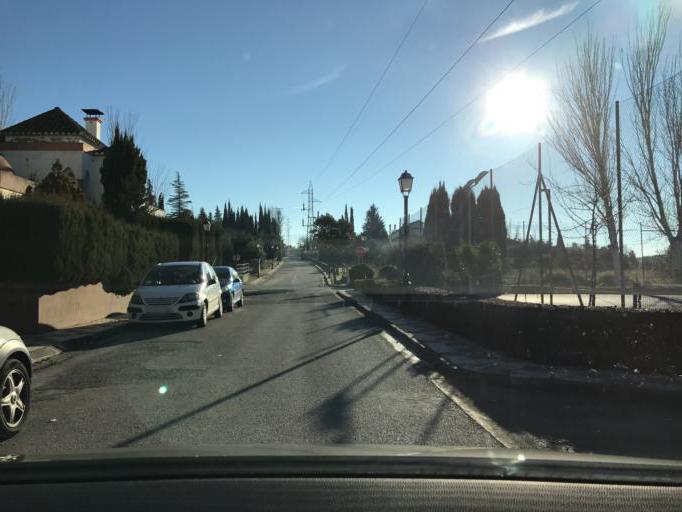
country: ES
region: Andalusia
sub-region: Provincia de Granada
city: Albolote
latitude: 37.2510
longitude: -3.6562
